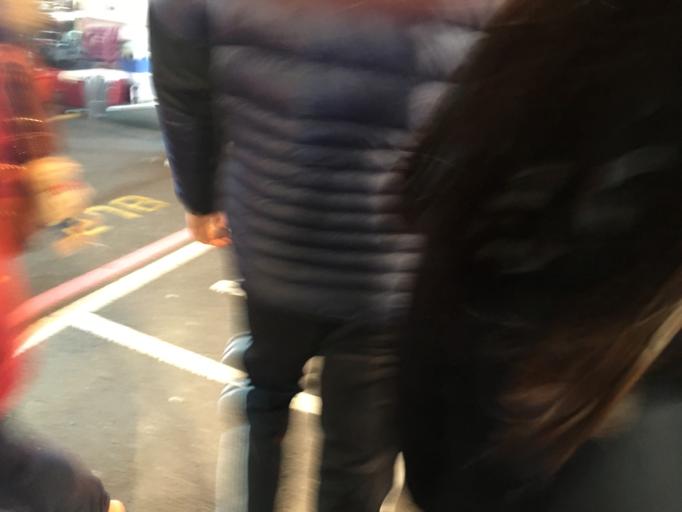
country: TW
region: Taiwan
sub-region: Hsinchu
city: Hsinchu
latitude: 24.8202
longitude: 120.9616
